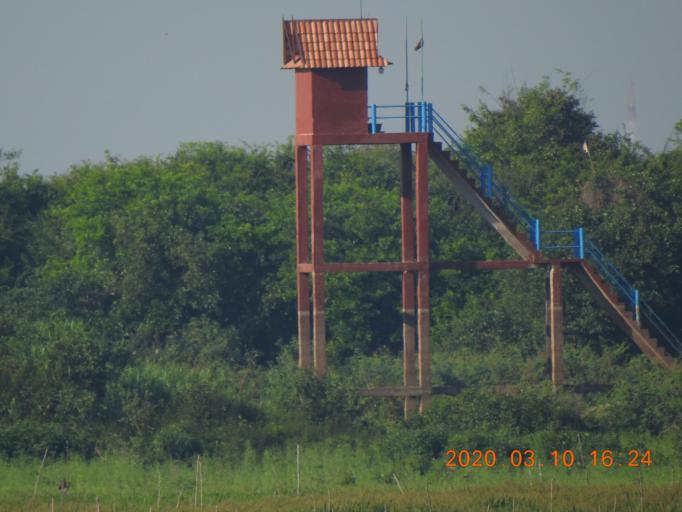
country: KH
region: Siem Reap
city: Siem Reap
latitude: 13.2255
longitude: 103.8250
